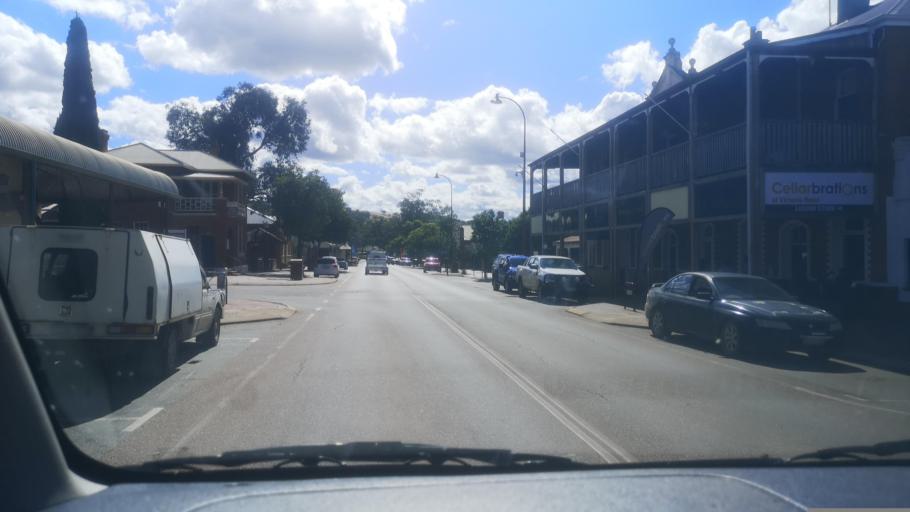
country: AU
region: Western Australia
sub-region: Toodyay
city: Toodyay
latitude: -31.5500
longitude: 116.4676
